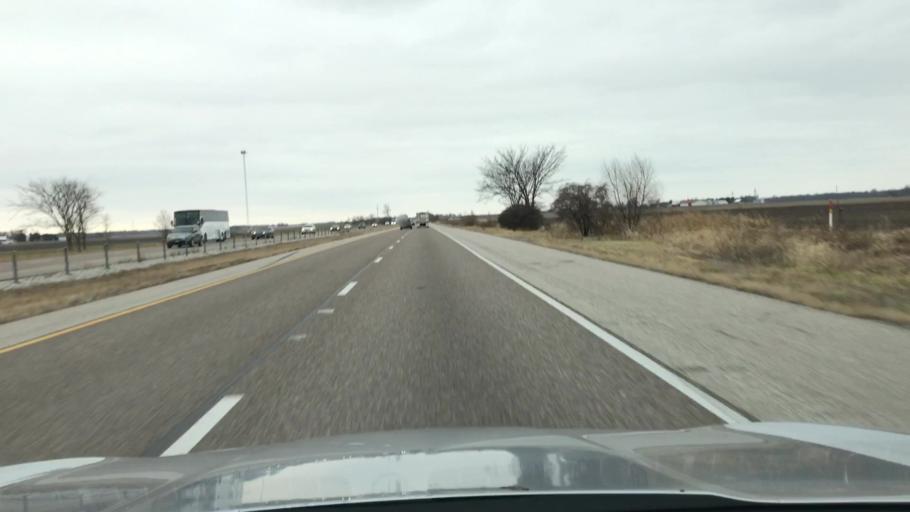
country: US
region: Illinois
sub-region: Madison County
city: Edwardsville
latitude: 38.8400
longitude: -89.8727
